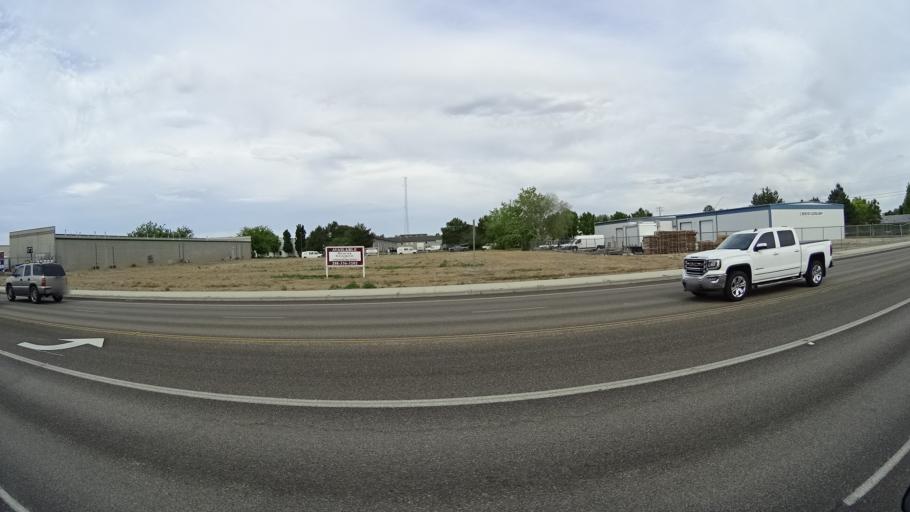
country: US
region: Idaho
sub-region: Ada County
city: Meridian
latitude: 43.6112
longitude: -116.3744
